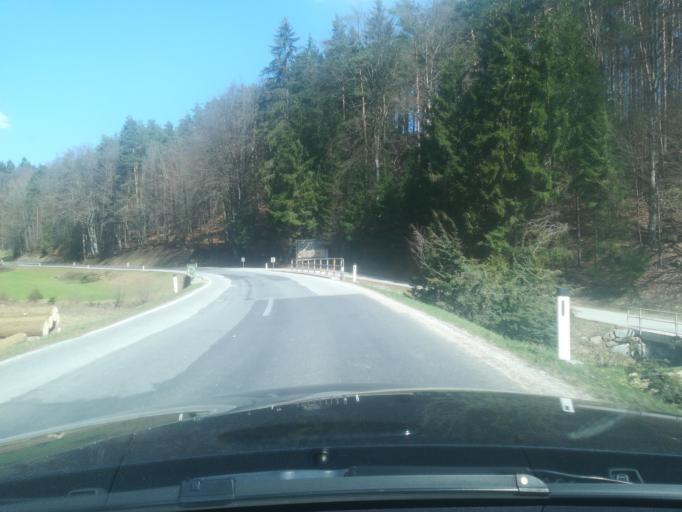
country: AT
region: Upper Austria
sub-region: Politischer Bezirk Perg
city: Bad Kreuzen
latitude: 48.3997
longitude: 14.7333
